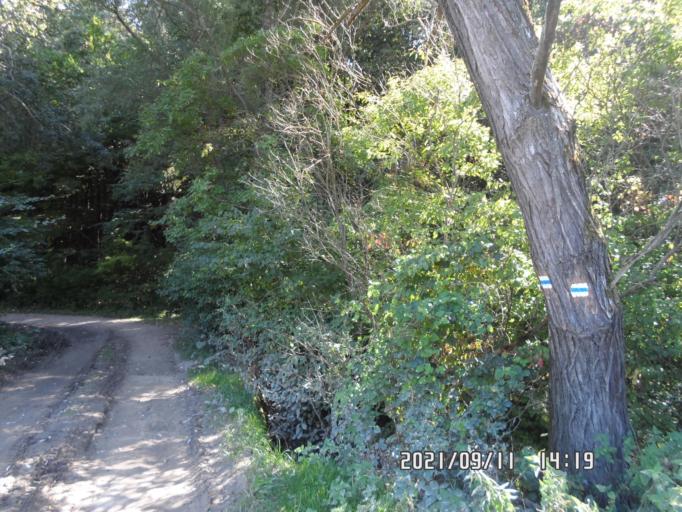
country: HU
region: Zala
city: Zalalovo
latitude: 46.7750
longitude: 16.6902
